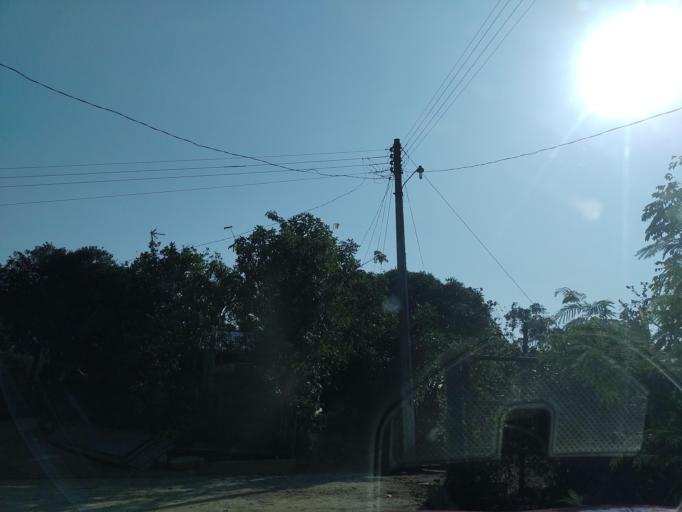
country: MX
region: Veracruz
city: Agua Dulce
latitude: 20.3680
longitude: -97.1856
